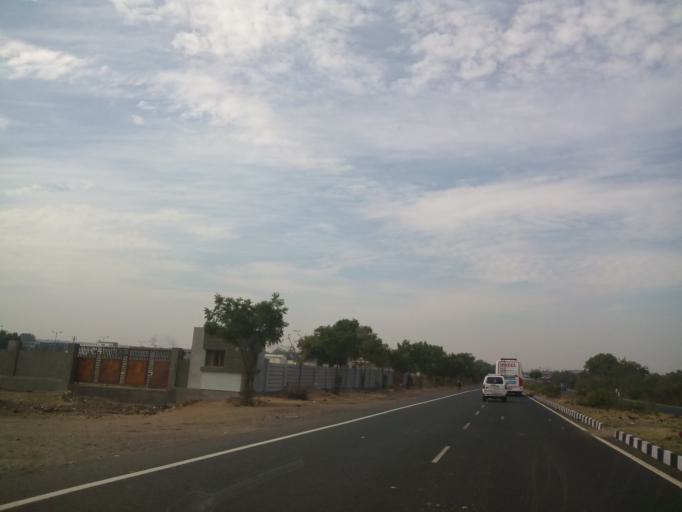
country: IN
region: Gujarat
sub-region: Rajkot
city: Rajkot
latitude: 22.3789
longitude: 70.9794
